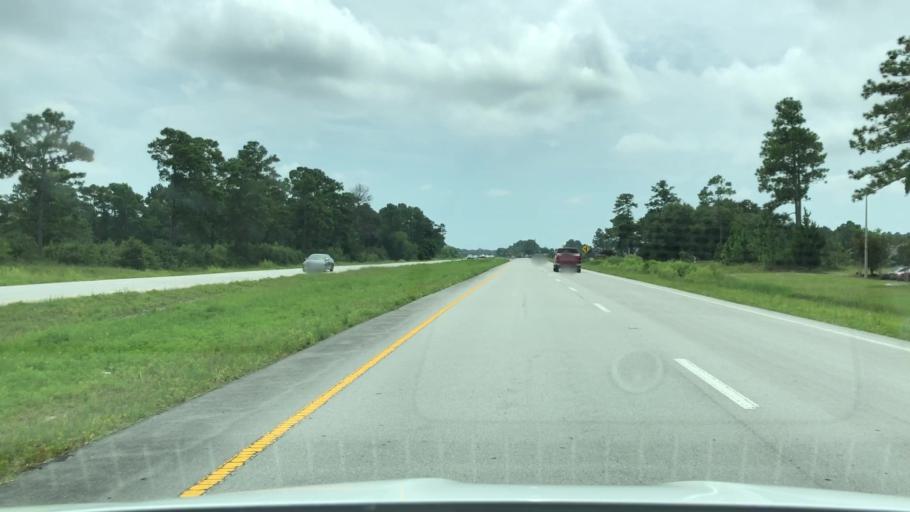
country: US
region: North Carolina
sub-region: Carteret County
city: Newport
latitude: 34.7964
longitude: -76.8778
